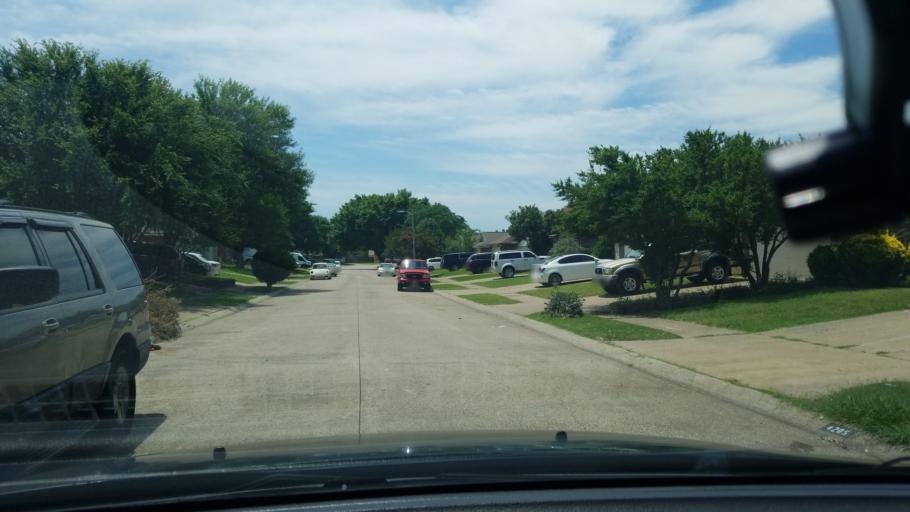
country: US
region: Texas
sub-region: Dallas County
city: Mesquite
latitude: 32.8026
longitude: -96.6601
